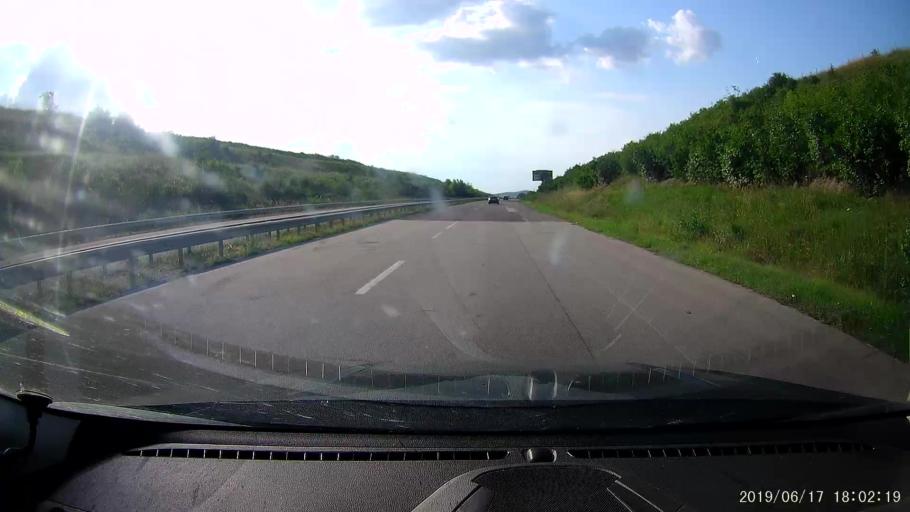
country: BG
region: Khaskovo
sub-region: Obshtina Svilengrad
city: Svilengrad
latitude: 41.7578
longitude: 26.2327
